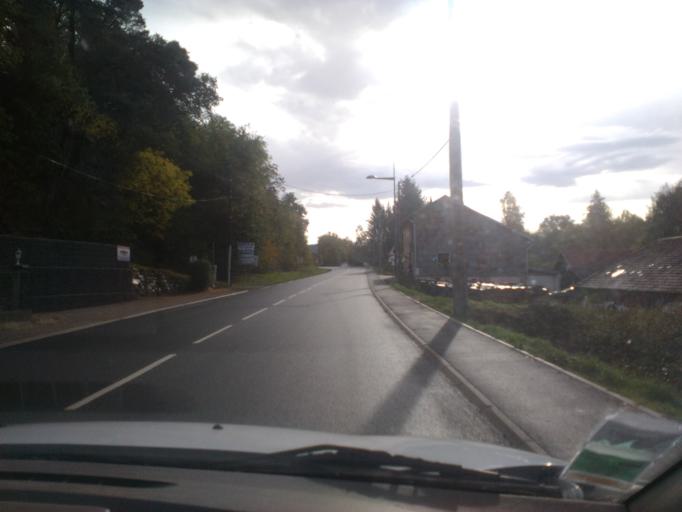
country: FR
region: Lorraine
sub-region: Departement des Vosges
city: Corcieux
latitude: 48.1676
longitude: 6.8913
